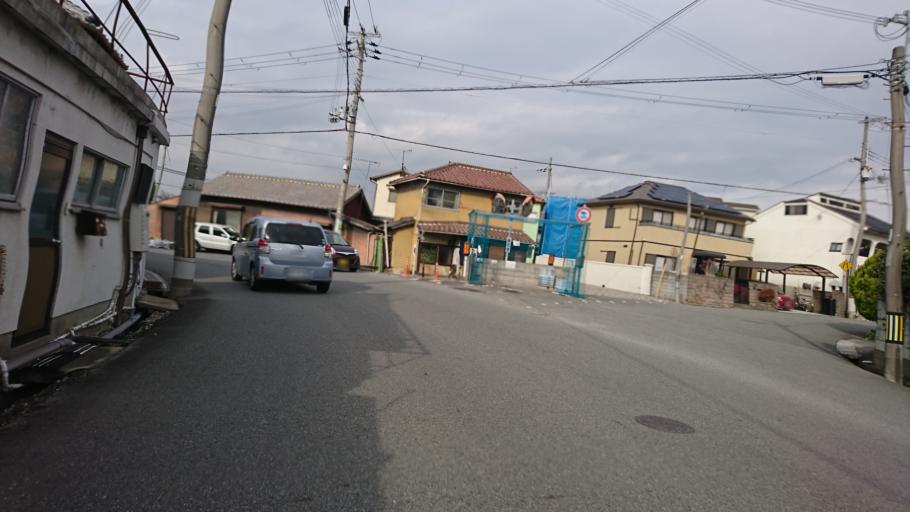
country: JP
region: Hyogo
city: Kakogawacho-honmachi
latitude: 34.7646
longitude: 134.8579
